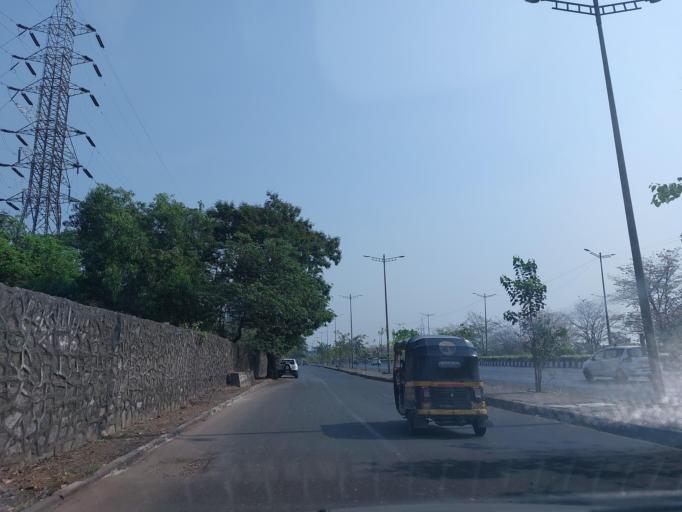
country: IN
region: Maharashtra
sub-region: Mumbai Suburban
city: Powai
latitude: 19.0962
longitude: 72.9268
